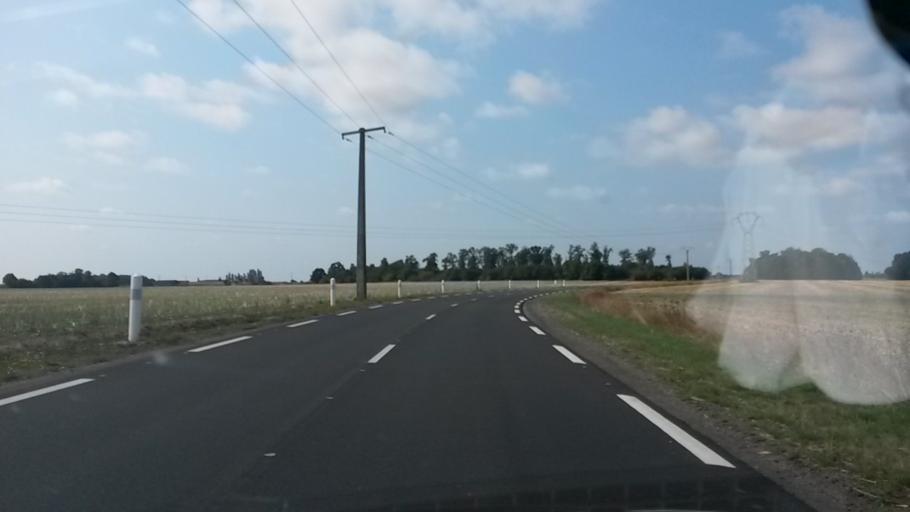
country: FR
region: Haute-Normandie
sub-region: Departement de l'Eure
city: Tillieres-sur-Avre
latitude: 48.7885
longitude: 0.9870
